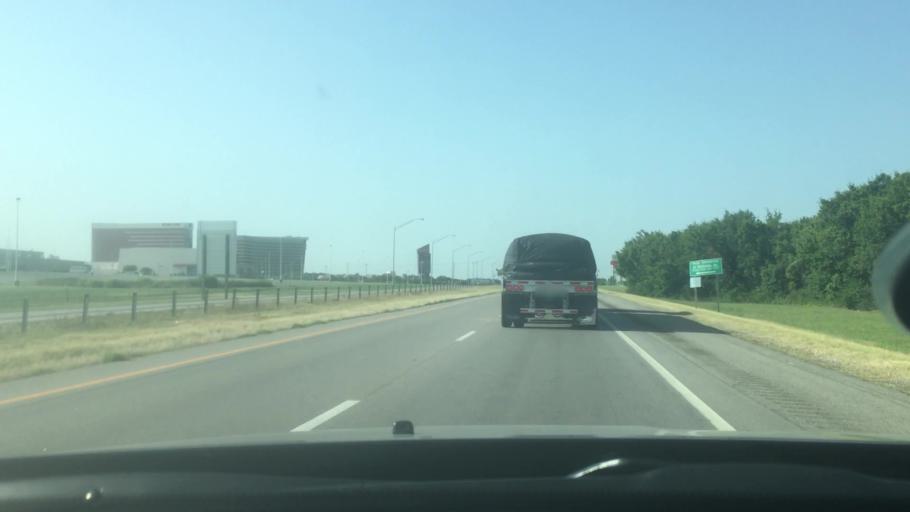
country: US
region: Oklahoma
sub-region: Bryan County
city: Calera
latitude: 33.9593
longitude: -96.4168
